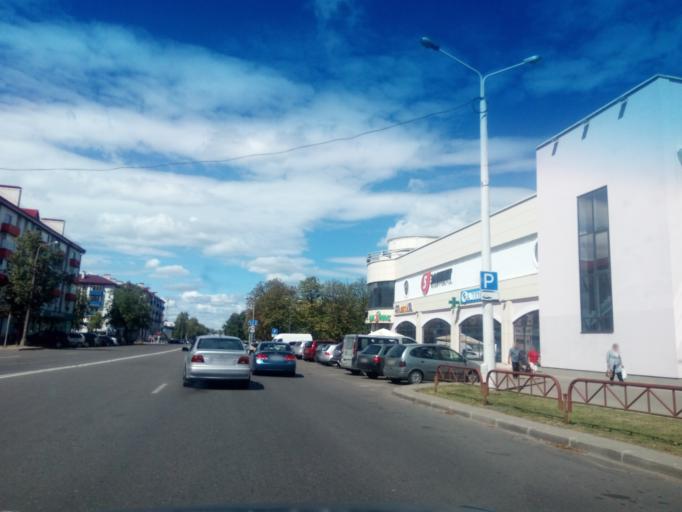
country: BY
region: Vitebsk
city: Polatsk
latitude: 55.4902
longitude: 28.7824
